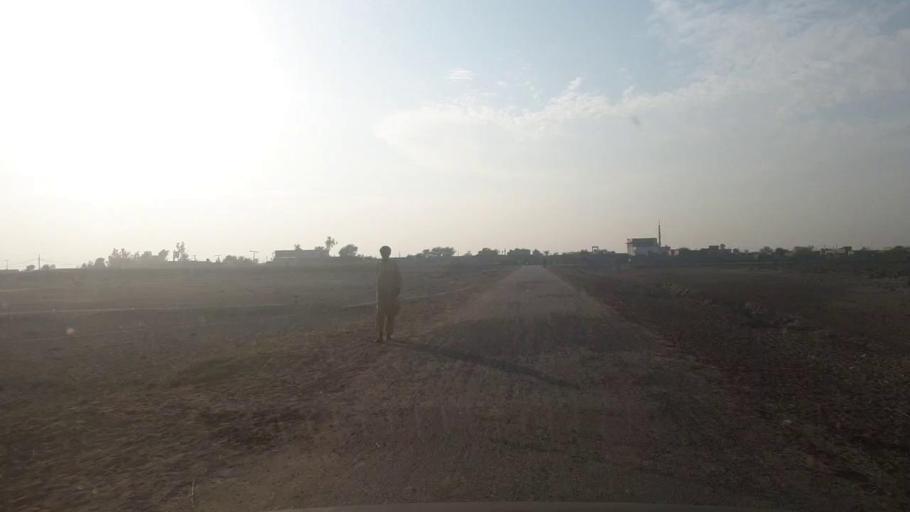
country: PK
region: Sindh
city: Sakrand
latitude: 26.0746
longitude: 68.4040
